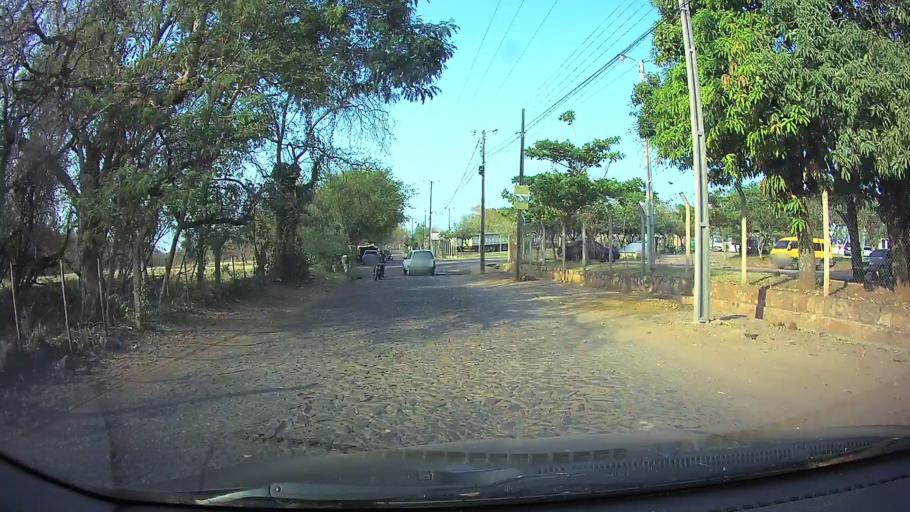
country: PY
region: Central
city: Limpio
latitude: -25.2255
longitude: -57.5083
